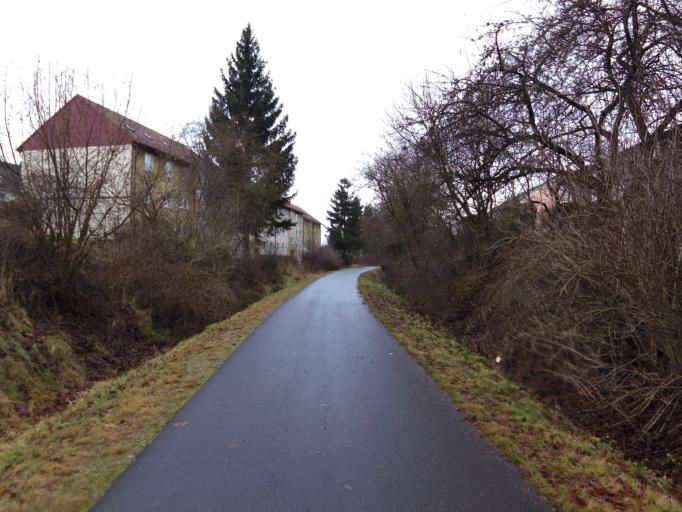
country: DE
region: Bavaria
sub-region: Upper Franconia
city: Wunsiedel
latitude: 50.0409
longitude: 12.0083
